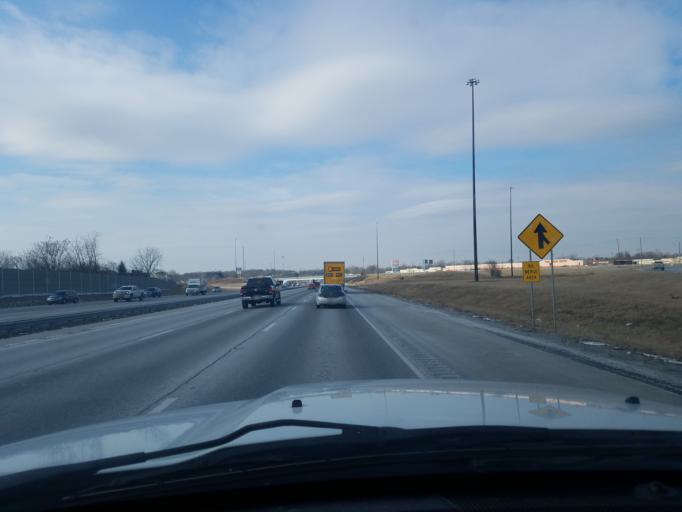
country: US
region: Indiana
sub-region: Marion County
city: Southport
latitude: 39.6630
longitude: -86.0857
